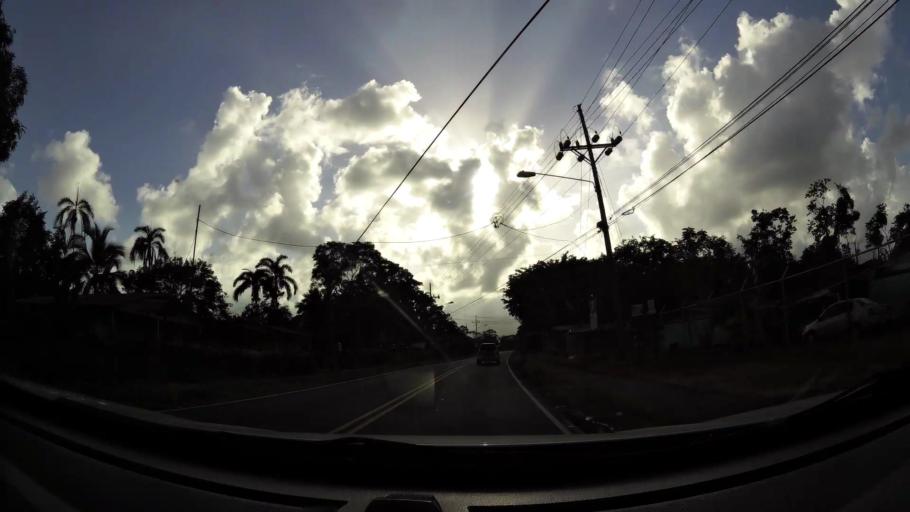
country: CR
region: Limon
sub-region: Canton de Siquirres
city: Siquirres
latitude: 10.0947
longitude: -83.5363
